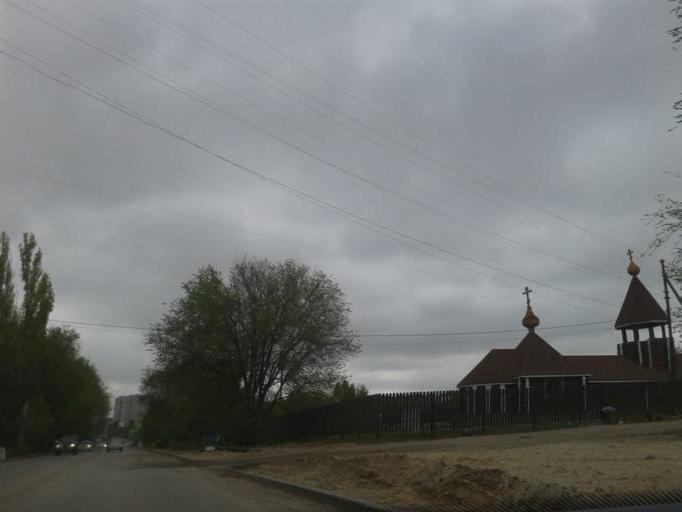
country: RU
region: Volgograd
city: Gorodishche
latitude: 48.7669
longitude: 44.4975
